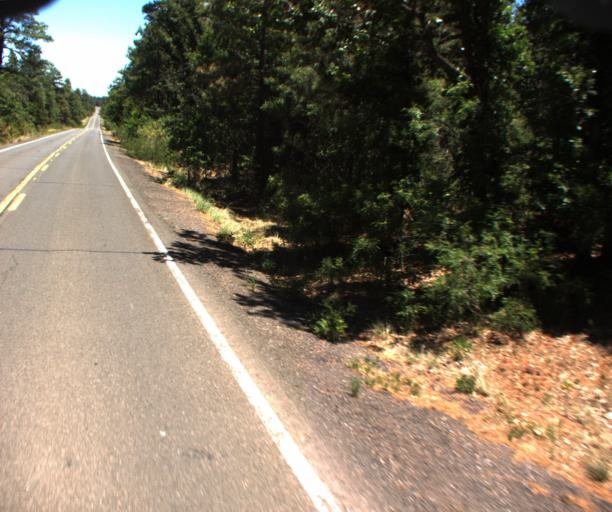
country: US
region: Arizona
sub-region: Gila County
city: Pine
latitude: 34.6074
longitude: -111.2135
